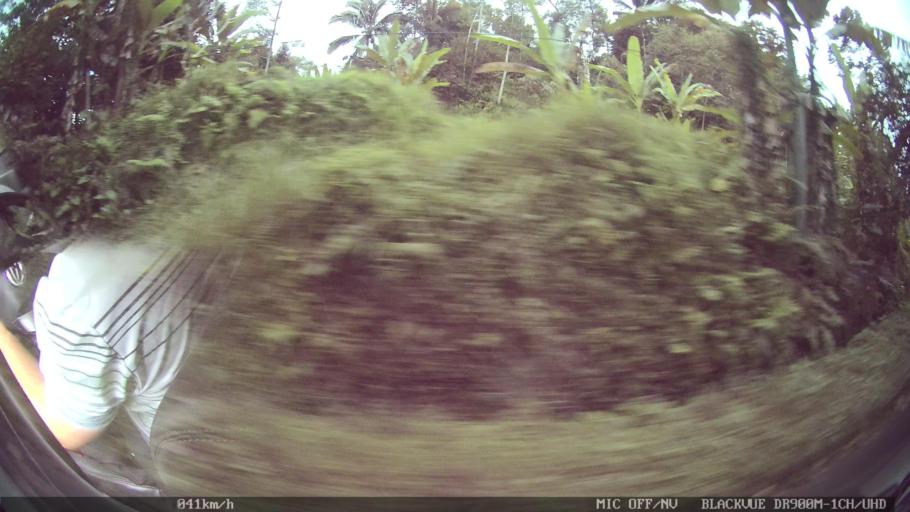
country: ID
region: Bali
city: Peneng
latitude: -8.3677
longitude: 115.2198
